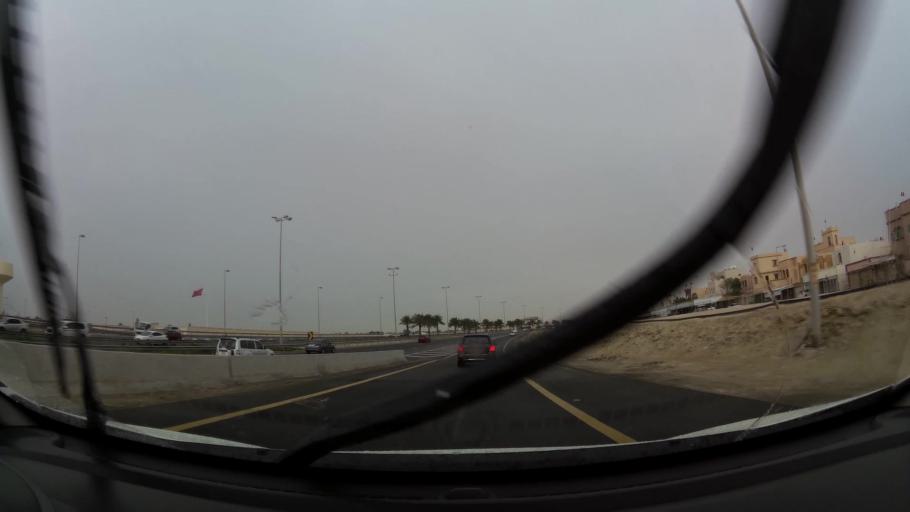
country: BH
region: Central Governorate
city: Madinat Hamad
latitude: 26.1180
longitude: 50.5097
